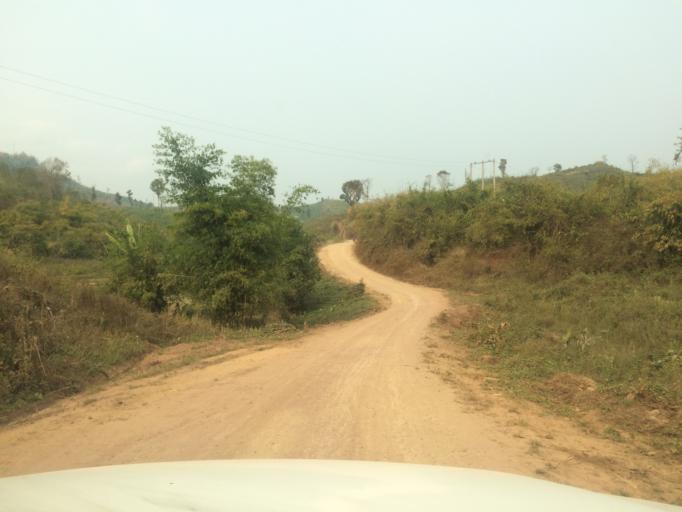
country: LA
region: Loungnamtha
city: Muang Nale
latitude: 20.4268
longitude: 101.7033
